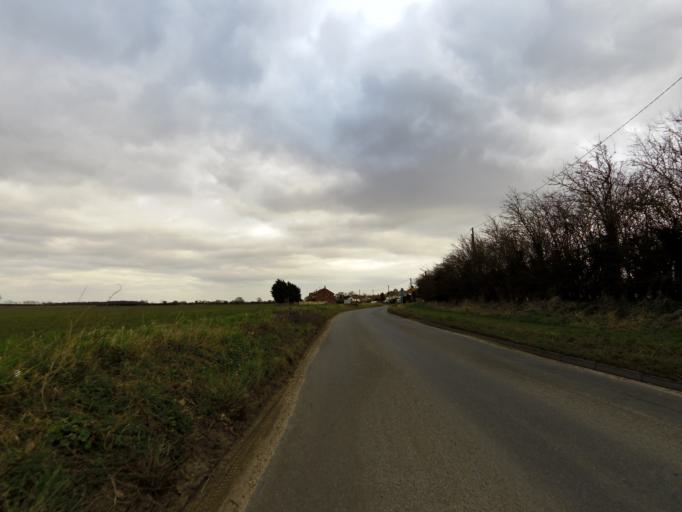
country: GB
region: England
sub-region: Suffolk
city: Felixstowe
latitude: 52.0146
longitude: 1.3103
